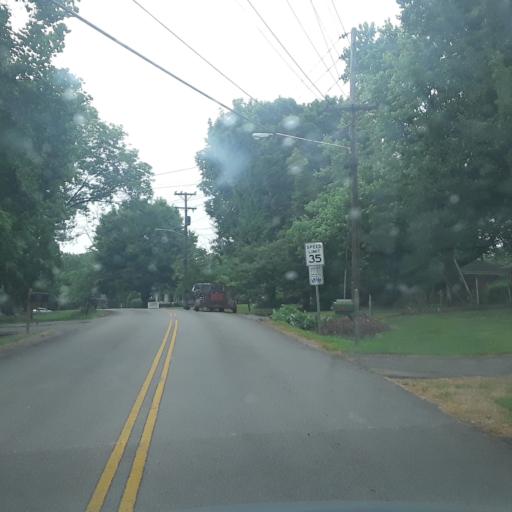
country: US
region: Tennessee
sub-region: Davidson County
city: Oak Hill
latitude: 36.0741
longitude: -86.7460
